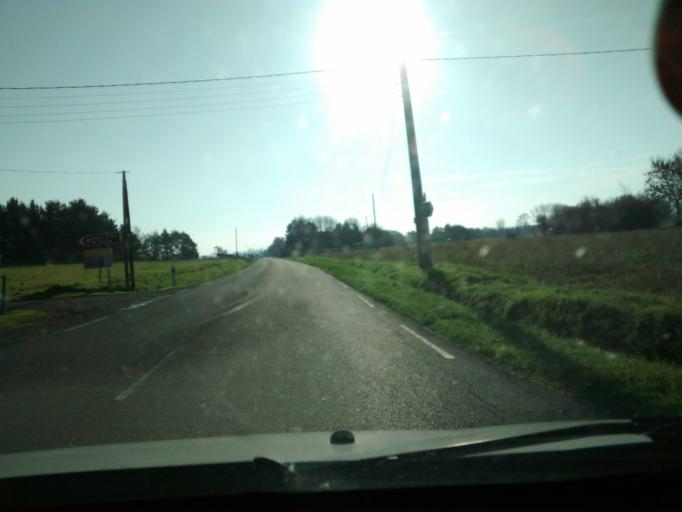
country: FR
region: Lower Normandy
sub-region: Departement de la Manche
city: Pontorson
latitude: 48.5842
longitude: -1.5114
